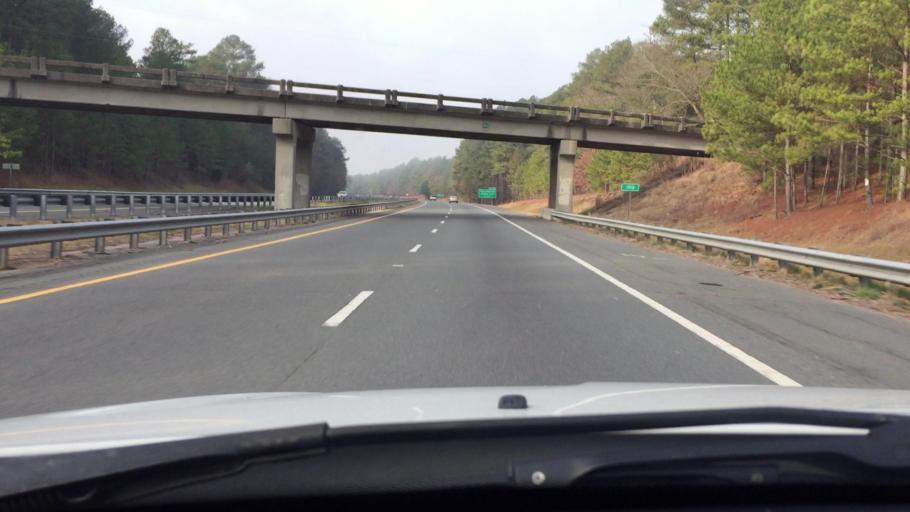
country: US
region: North Carolina
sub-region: Wake County
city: Green Level
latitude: 35.6448
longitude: -79.0134
